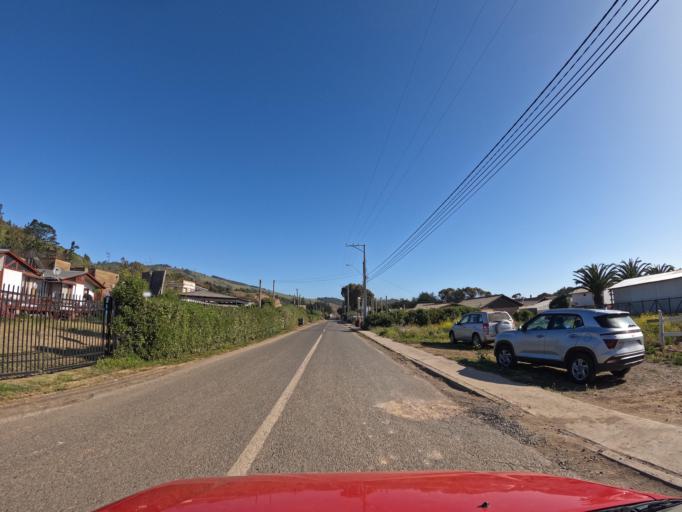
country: CL
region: Maule
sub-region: Provincia de Talca
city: Constitucion
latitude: -34.8468
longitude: -72.1412
